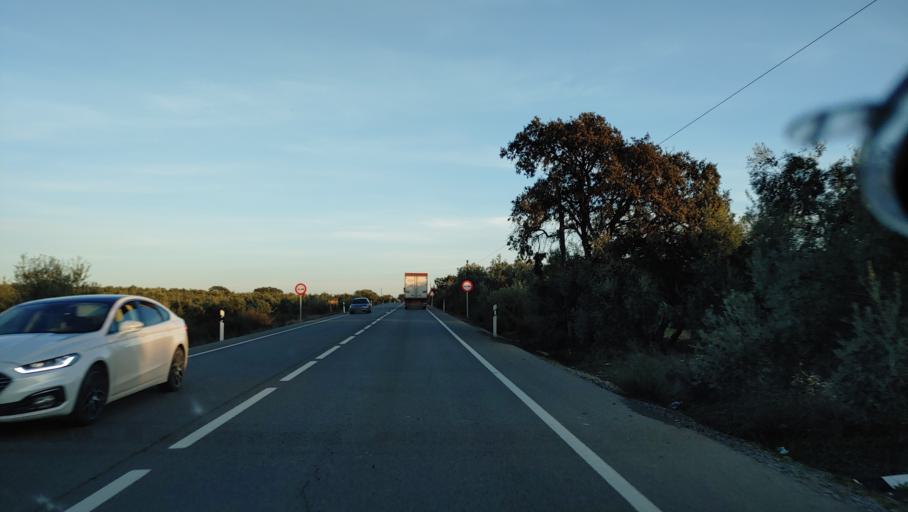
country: ES
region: Andalusia
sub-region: Provincia de Malaga
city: Humilladero
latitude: 37.0577
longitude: -4.6792
